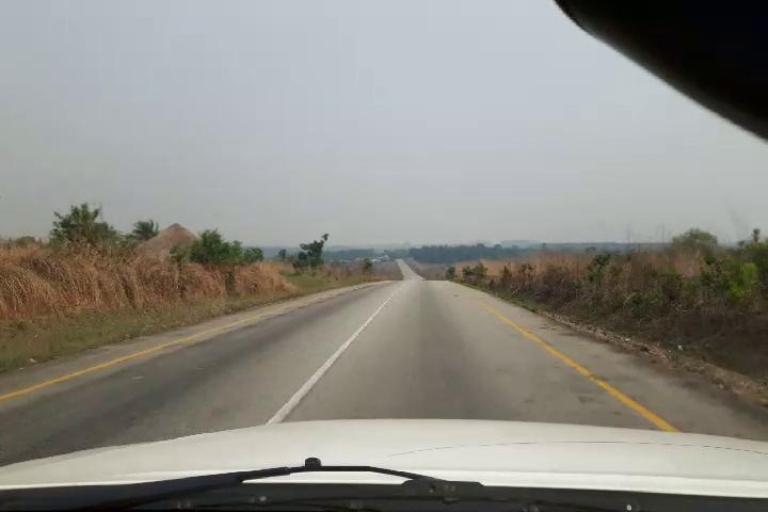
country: SL
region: Southern Province
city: Largo
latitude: 8.2268
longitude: -12.0771
